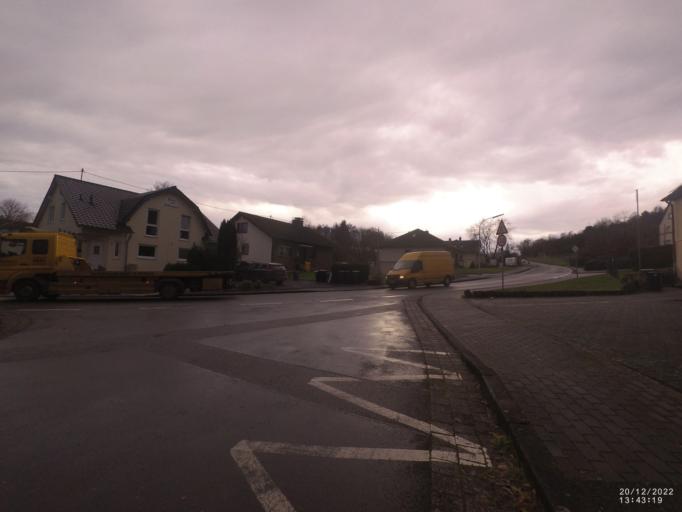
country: DE
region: Rheinland-Pfalz
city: Sinzig
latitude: 50.5370
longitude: 7.2248
